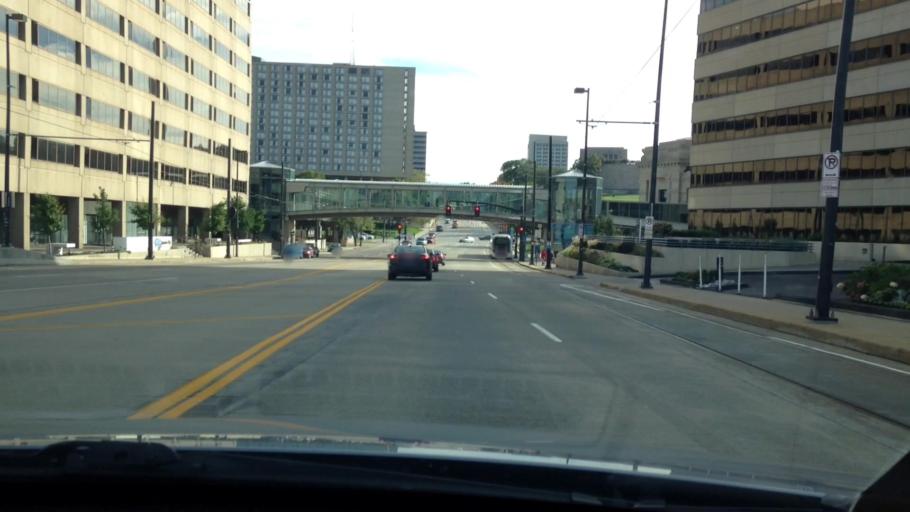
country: US
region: Missouri
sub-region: Jackson County
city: Kansas City
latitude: 39.0863
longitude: -94.5840
